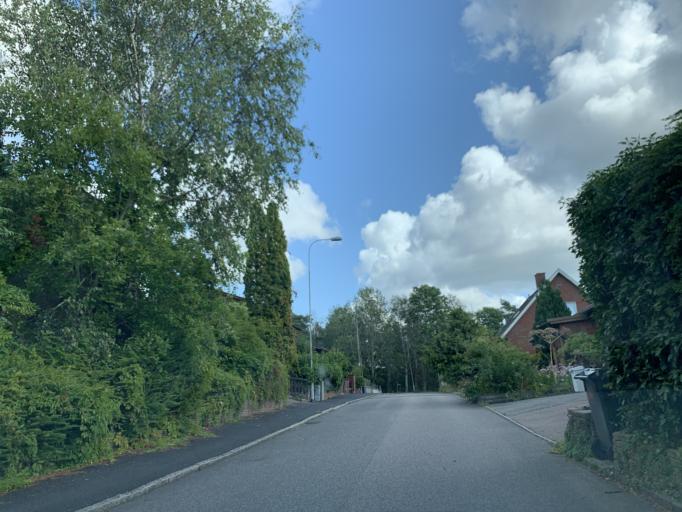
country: SE
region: Vaestra Goetaland
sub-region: Goteborg
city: Hammarkullen
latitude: 57.7757
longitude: 12.0264
